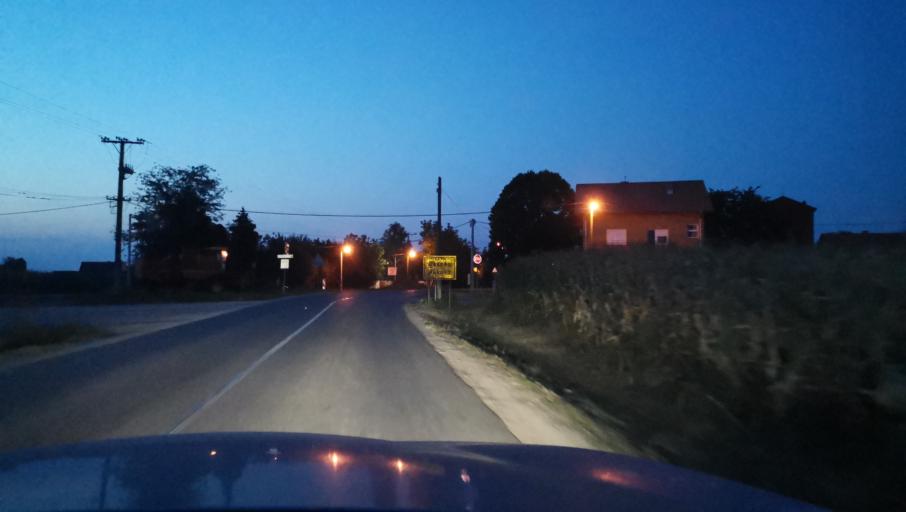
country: RS
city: Boljevci
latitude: 44.7429
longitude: 20.2527
